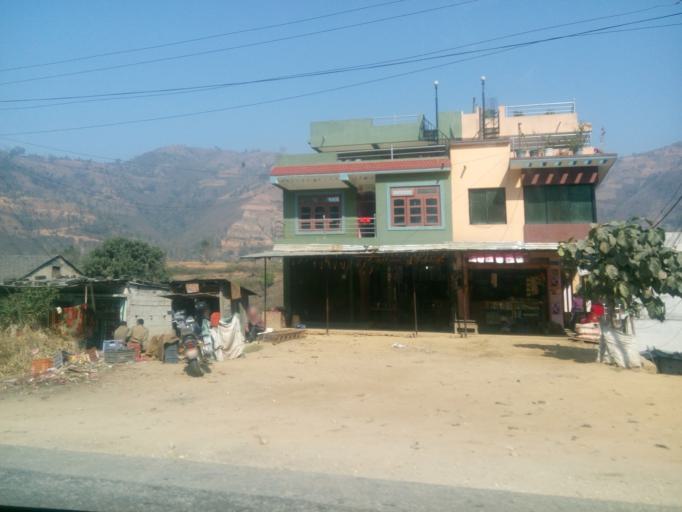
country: NP
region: Central Region
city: Kirtipur
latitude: 27.8053
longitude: 84.9039
